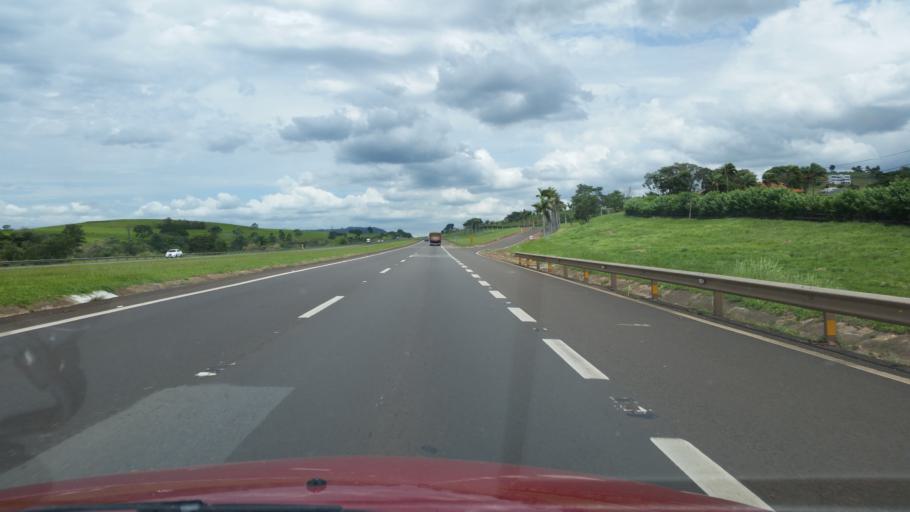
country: BR
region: Sao Paulo
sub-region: Itatinga
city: Itatinga
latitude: -23.1411
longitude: -48.4286
